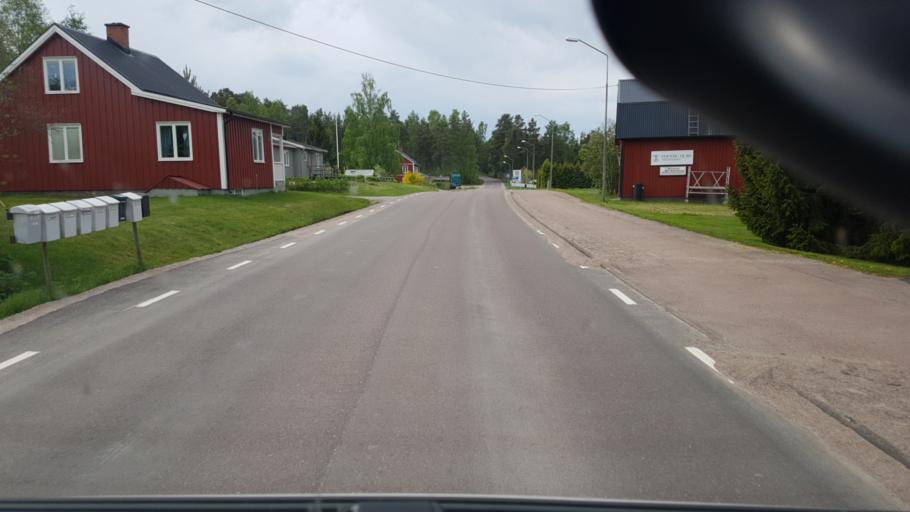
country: SE
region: Vaermland
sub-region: Arvika Kommun
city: Arvika
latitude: 59.5391
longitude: 12.7446
